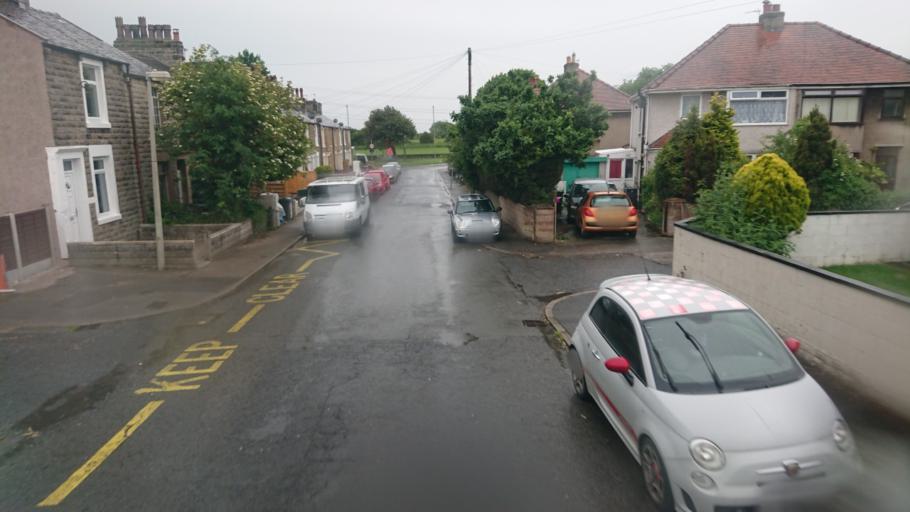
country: GB
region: England
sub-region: Lancashire
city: Morecambe
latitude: 54.0365
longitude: -2.8976
